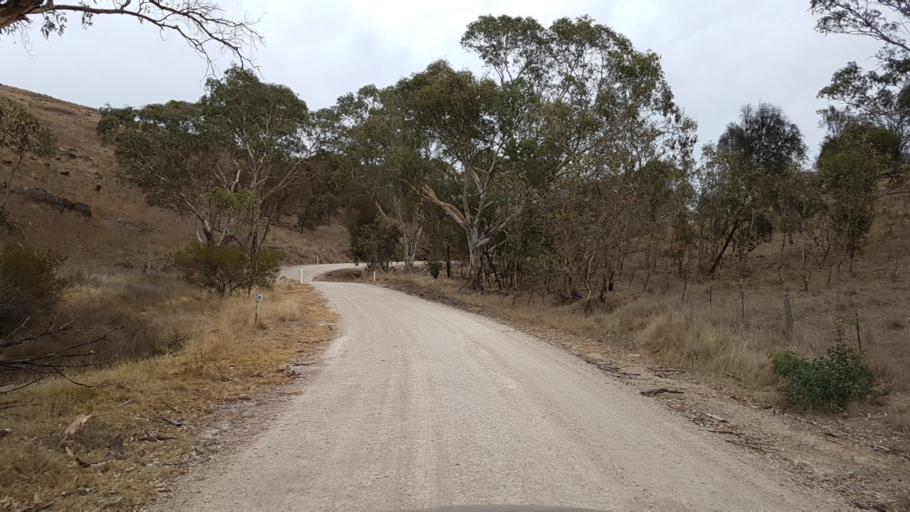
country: AU
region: South Australia
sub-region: Mount Barker
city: Callington
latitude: -35.0046
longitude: 139.0298
